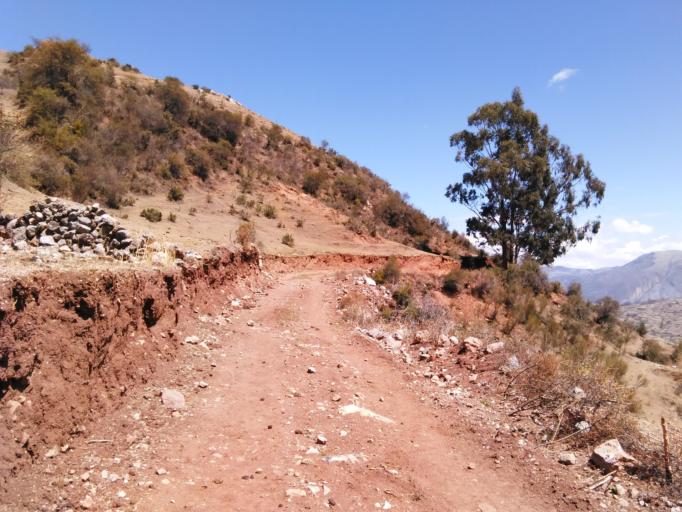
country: PE
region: Ayacucho
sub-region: Provincia de Victor Fajardo
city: Canaria
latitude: -13.8843
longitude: -73.9473
